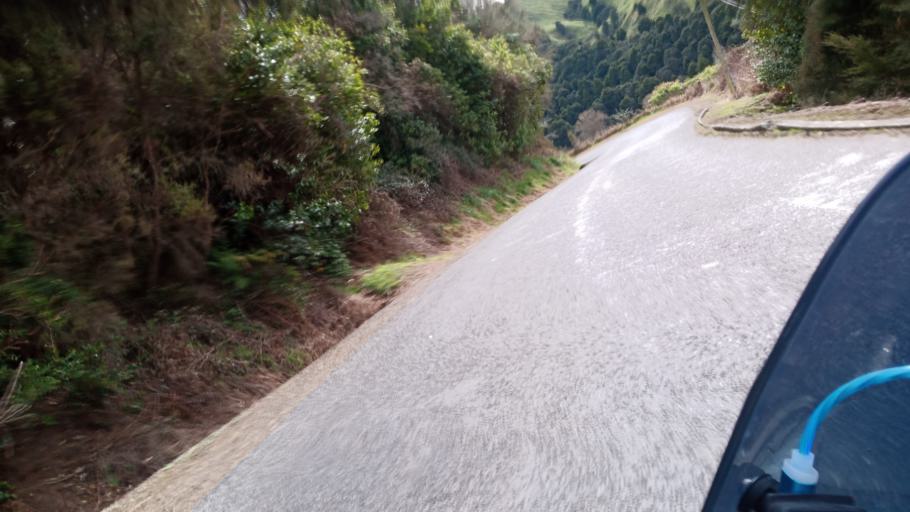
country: NZ
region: Hawke's Bay
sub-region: Wairoa District
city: Wairoa
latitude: -38.8010
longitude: 177.4698
